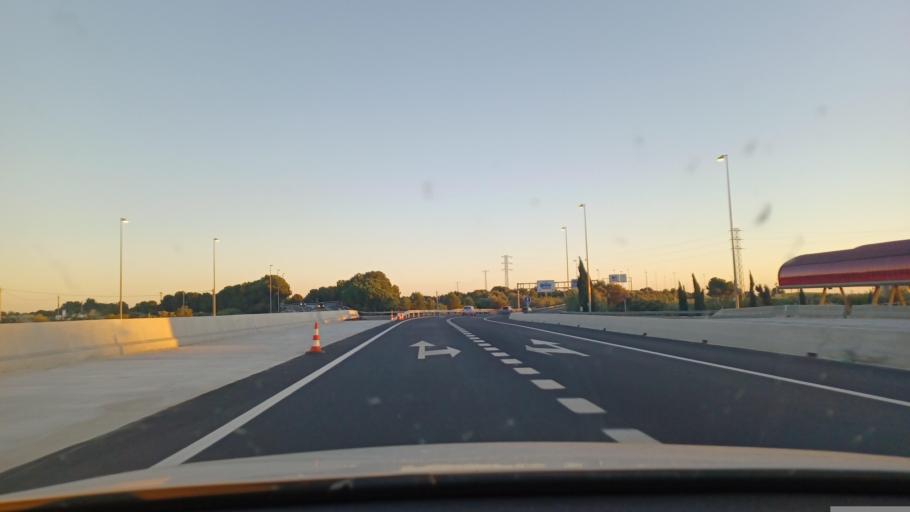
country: ES
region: Catalonia
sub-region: Provincia de Tarragona
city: Vila-seca
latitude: 41.1081
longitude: 1.1308
